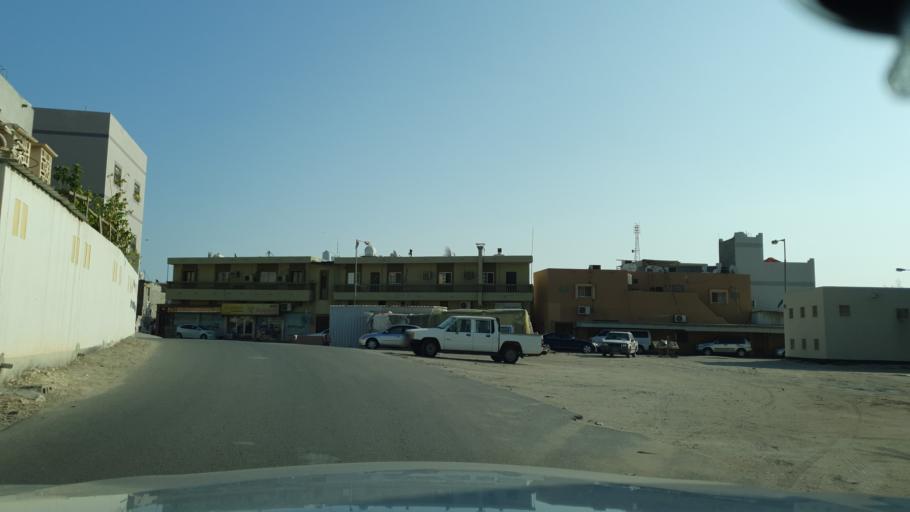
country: BH
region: Manama
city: Jidd Hafs
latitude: 26.2190
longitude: 50.4637
